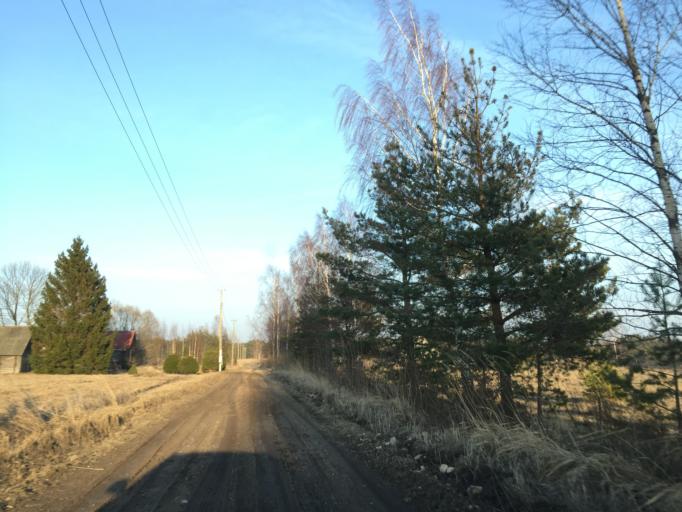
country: EE
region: Laeaene
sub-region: Lihula vald
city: Lihula
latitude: 58.4563
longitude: 23.7392
